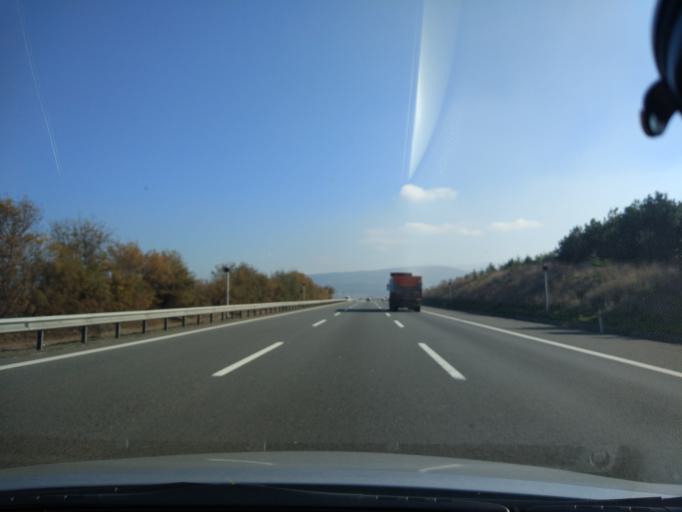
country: TR
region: Bolu
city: Bolu
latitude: 40.7680
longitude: 31.7446
